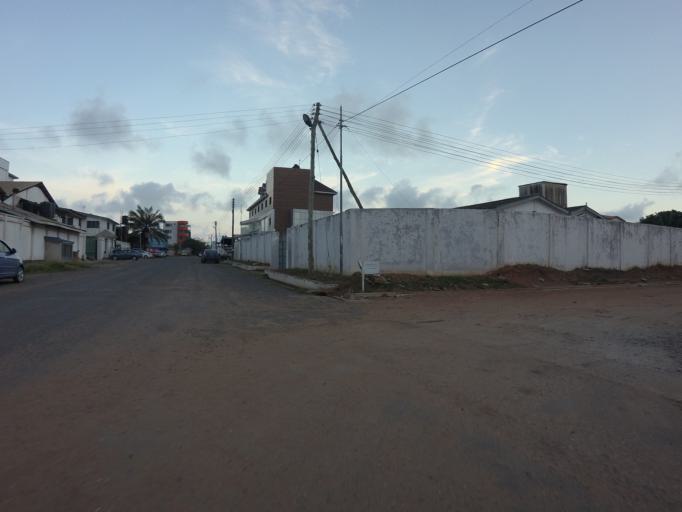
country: GH
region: Greater Accra
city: Accra
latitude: 5.5607
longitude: -0.1718
